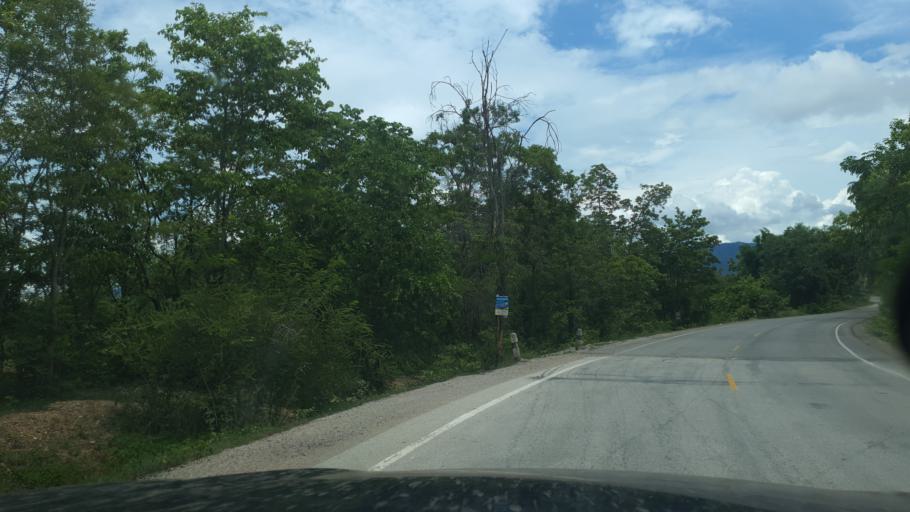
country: TH
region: Lampang
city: Sop Prap
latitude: 17.9294
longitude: 99.3725
